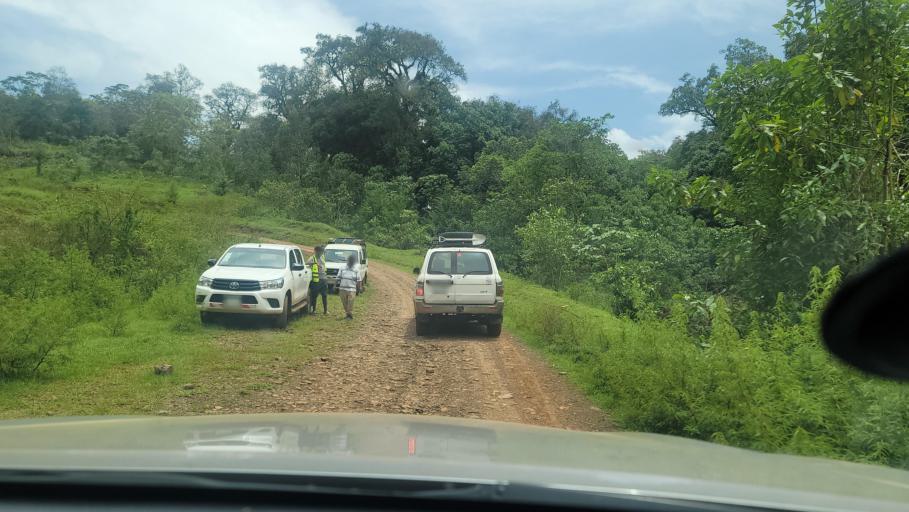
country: ET
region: Southern Nations, Nationalities, and People's Region
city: Bonga
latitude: 7.6386
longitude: 36.2260
